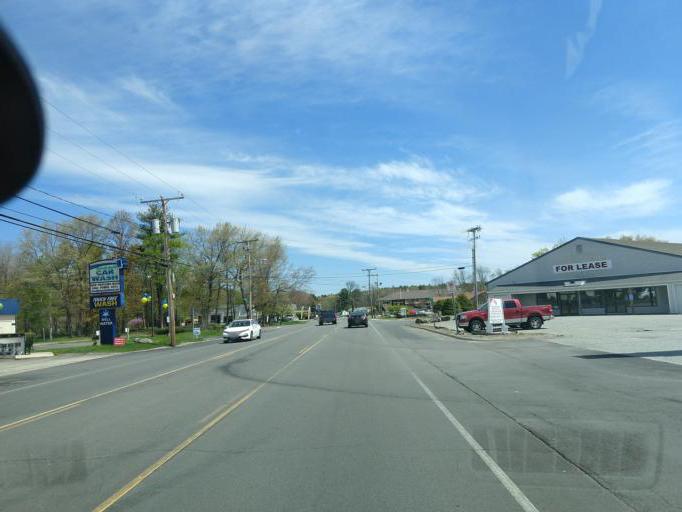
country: US
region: New Hampshire
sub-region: Rockingham County
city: Seabrook
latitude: 42.9027
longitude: -70.8682
